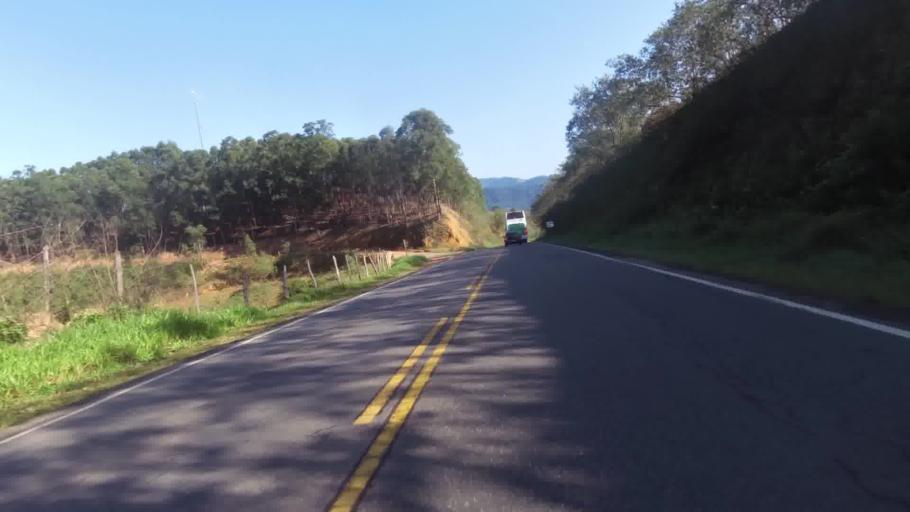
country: BR
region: Espirito Santo
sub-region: Alfredo Chaves
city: Alfredo Chaves
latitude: -20.6673
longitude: -40.7375
